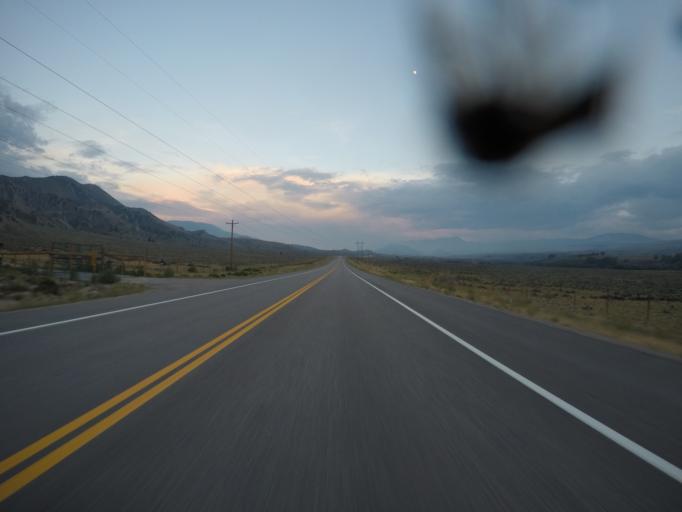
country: US
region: Colorado
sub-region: Grand County
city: Kremmling
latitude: 39.9873
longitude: -106.3588
